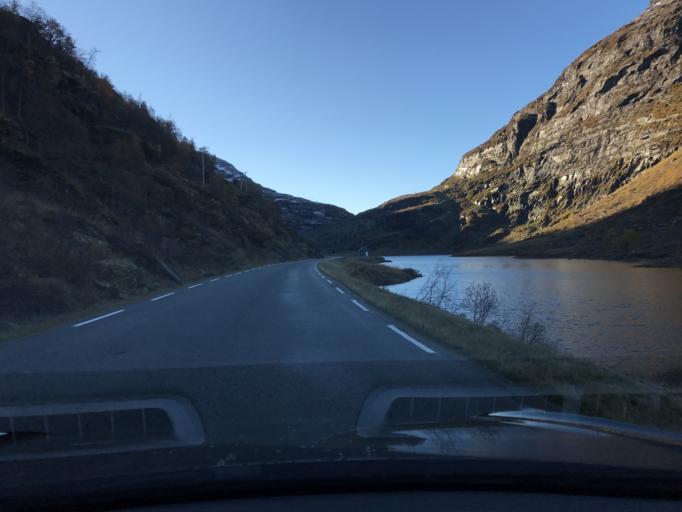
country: NO
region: Sogn og Fjordane
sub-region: Laerdal
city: Laerdalsoyri
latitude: 60.8100
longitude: 7.5581
